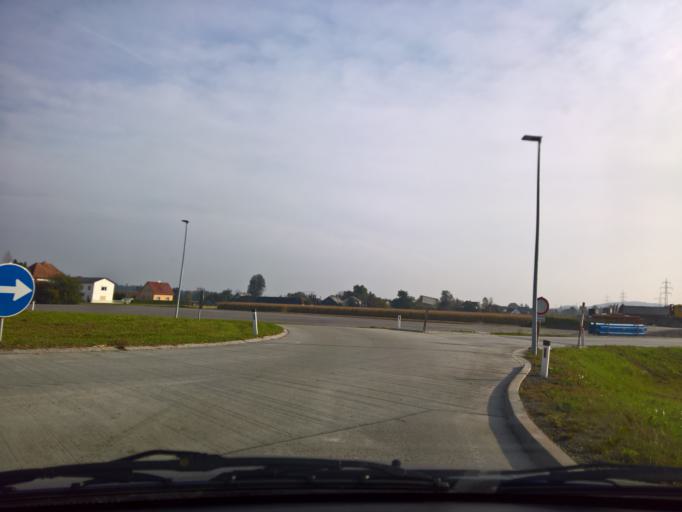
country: AT
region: Styria
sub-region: Politischer Bezirk Deutschlandsberg
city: Gross Sankt Florian
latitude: 46.8158
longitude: 15.3160
